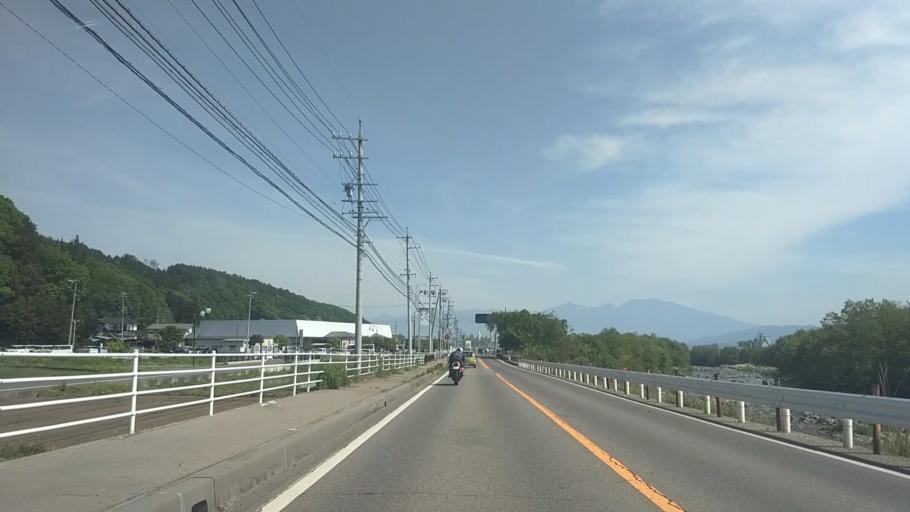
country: JP
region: Nagano
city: Saku
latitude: 36.1692
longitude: 138.4860
